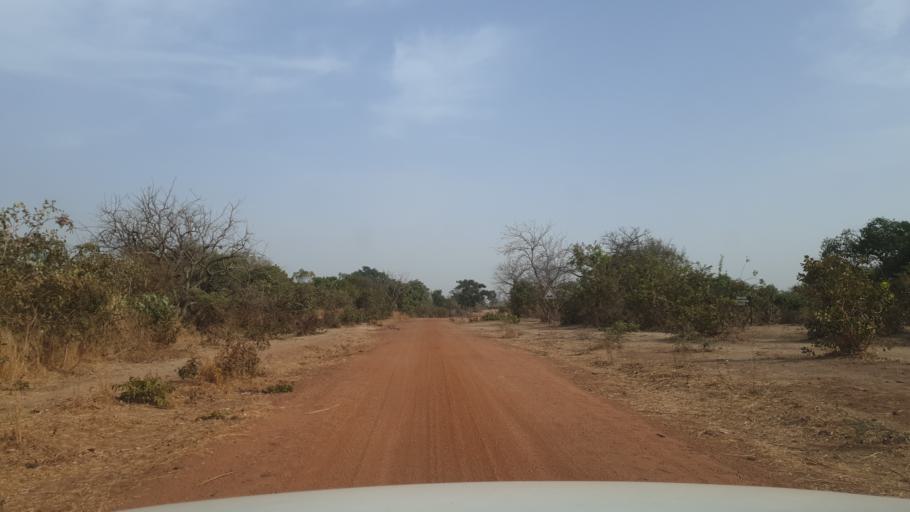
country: ML
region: Koulikoro
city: Kolokani
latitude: 13.3157
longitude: -8.2778
